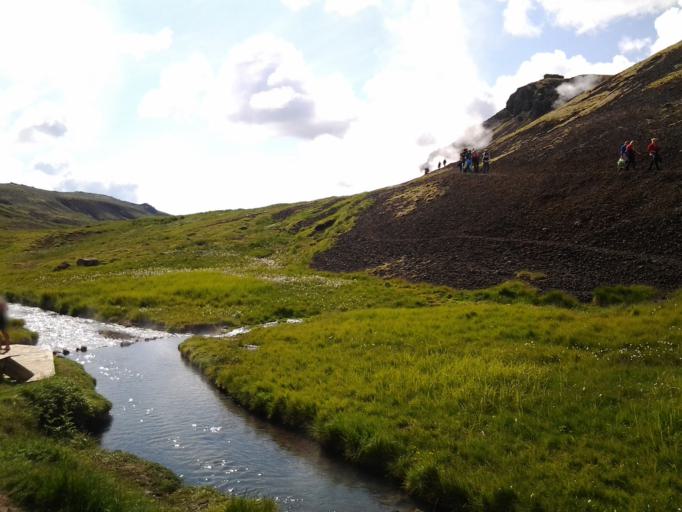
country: IS
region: South
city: Hveragerdi
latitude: 64.0474
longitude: -21.2216
